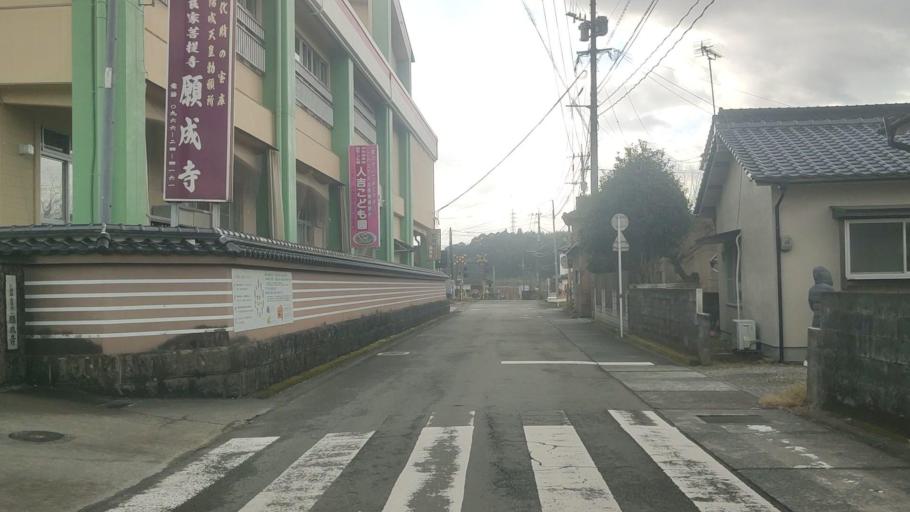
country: JP
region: Kumamoto
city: Hitoyoshi
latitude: 32.2182
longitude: 130.7718
